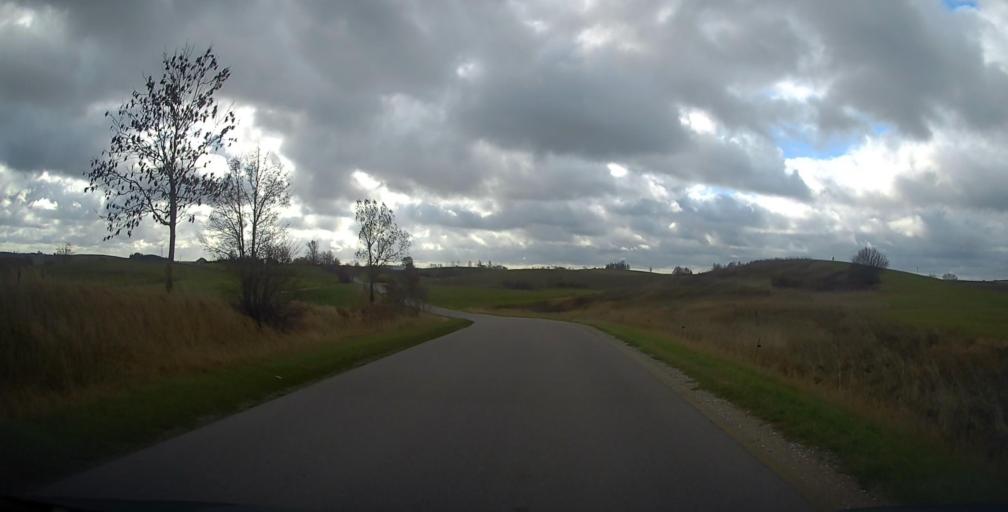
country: PL
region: Podlasie
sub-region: Suwalki
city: Suwalki
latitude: 54.3595
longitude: 22.8557
